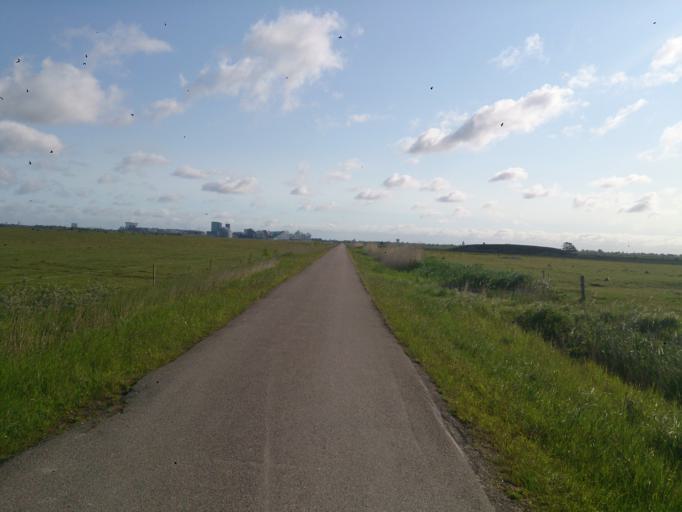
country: DK
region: Capital Region
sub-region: Tarnby Kommune
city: Tarnby
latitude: 55.6000
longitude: 12.5520
